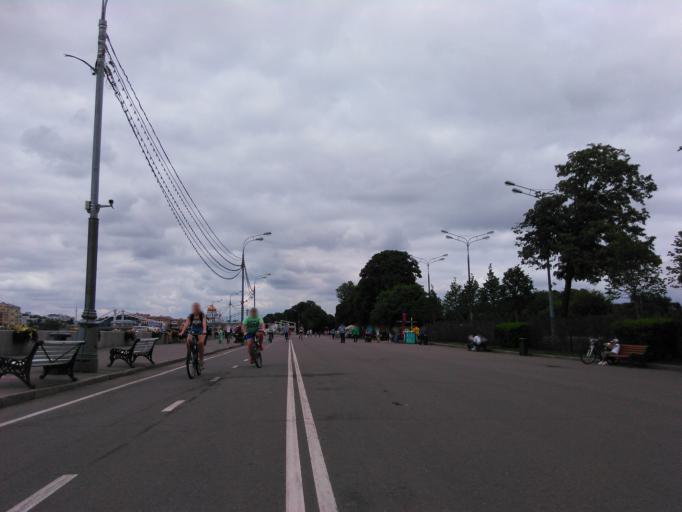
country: RU
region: Moscow
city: Novyye Cheremushki
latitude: 55.7272
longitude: 37.5959
